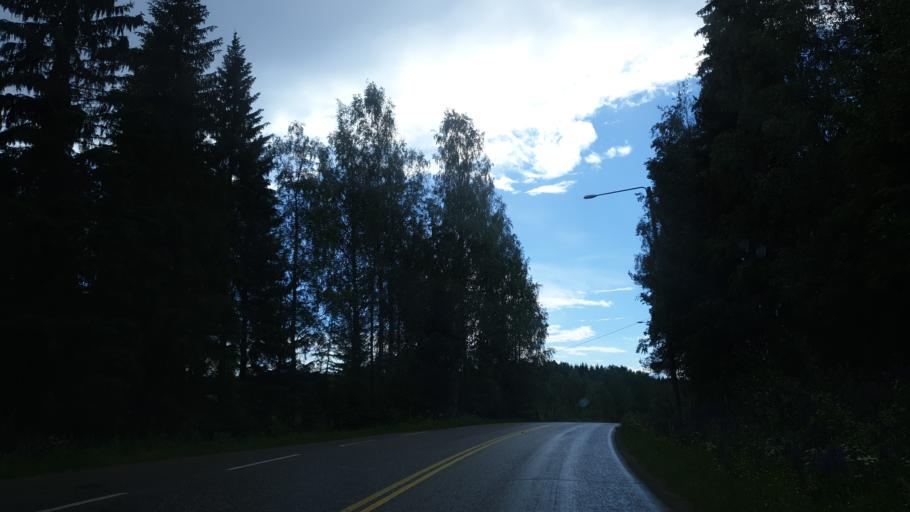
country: FI
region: Northern Savo
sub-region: Kuopio
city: Kuopio
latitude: 62.9095
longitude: 27.8636
